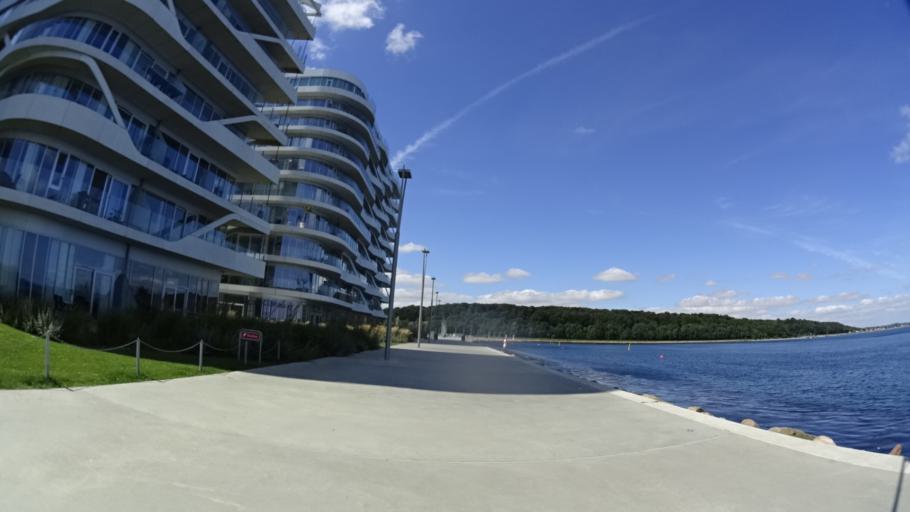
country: DK
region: Central Jutland
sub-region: Arhus Kommune
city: Arhus
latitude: 56.1665
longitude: 10.2306
